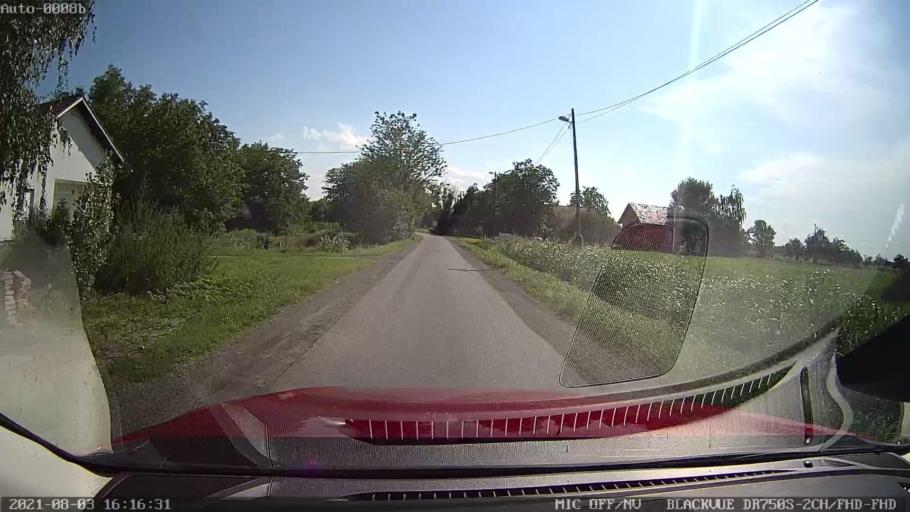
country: HR
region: Osjecko-Baranjska
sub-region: Grad Osijek
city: Bilje
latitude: 45.6021
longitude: 18.7826
